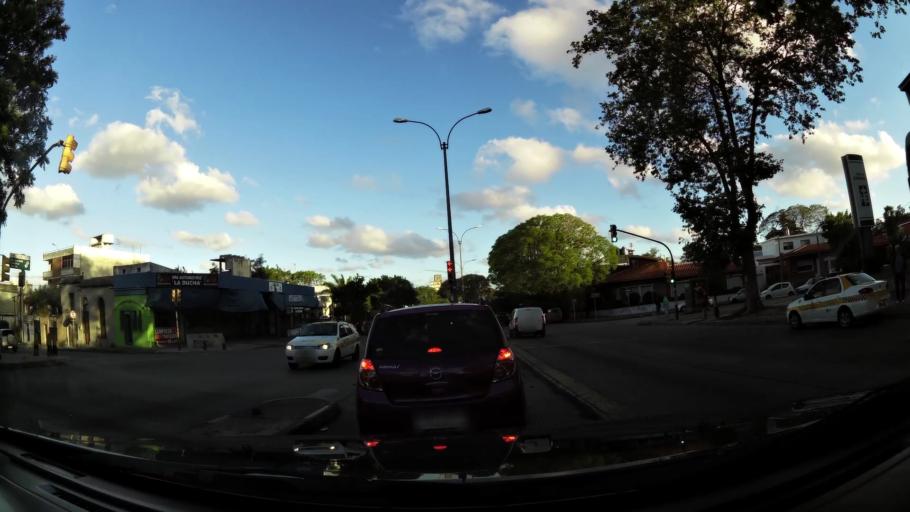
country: UY
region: Montevideo
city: Montevideo
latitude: -34.8806
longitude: -56.1462
